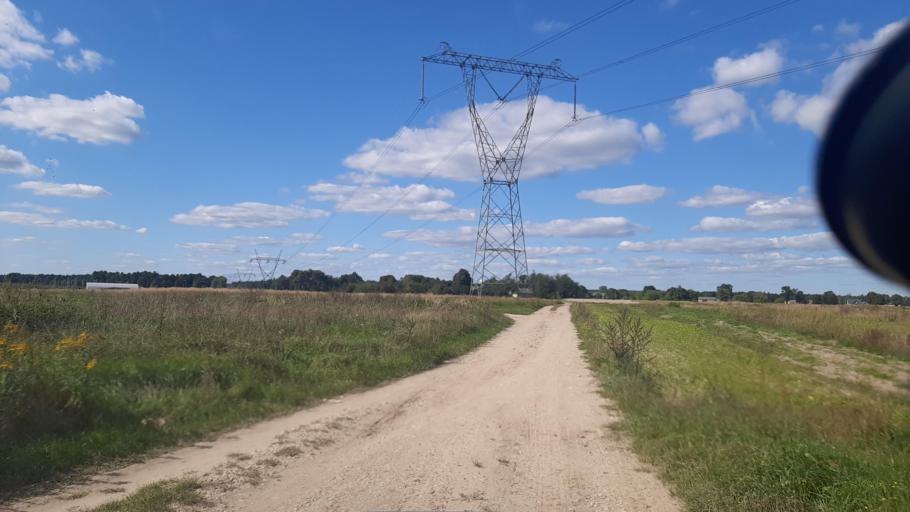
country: PL
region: Lublin Voivodeship
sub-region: Powiat pulawski
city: Kurow
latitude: 51.4031
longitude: 22.2115
